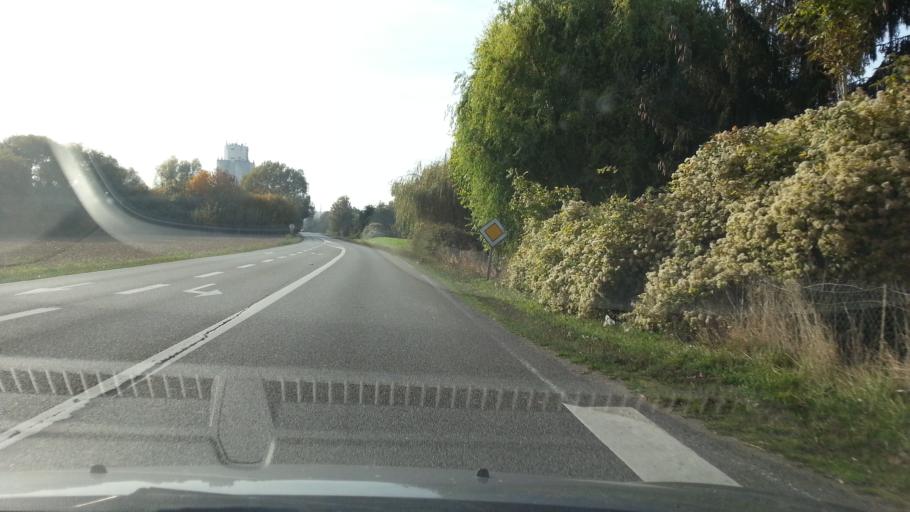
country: FR
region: Picardie
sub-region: Departement de l'Oise
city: Villers-sous-Saint-Leu
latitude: 49.2058
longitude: 2.3884
